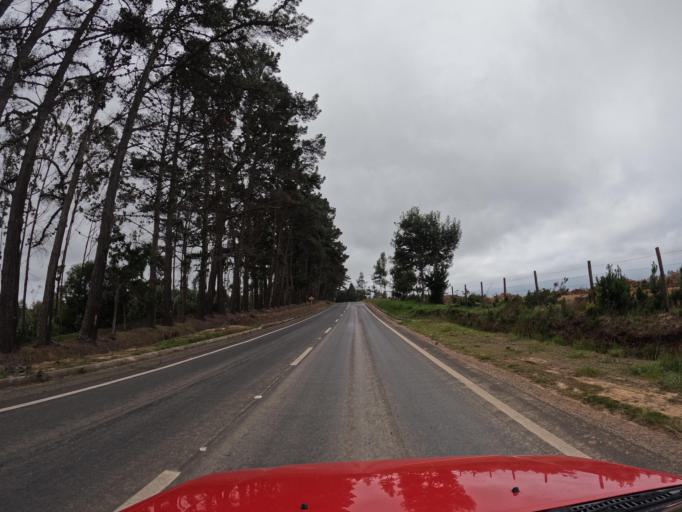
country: CL
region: O'Higgins
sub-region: Provincia de Colchagua
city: Santa Cruz
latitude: -34.5695
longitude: -72.0150
